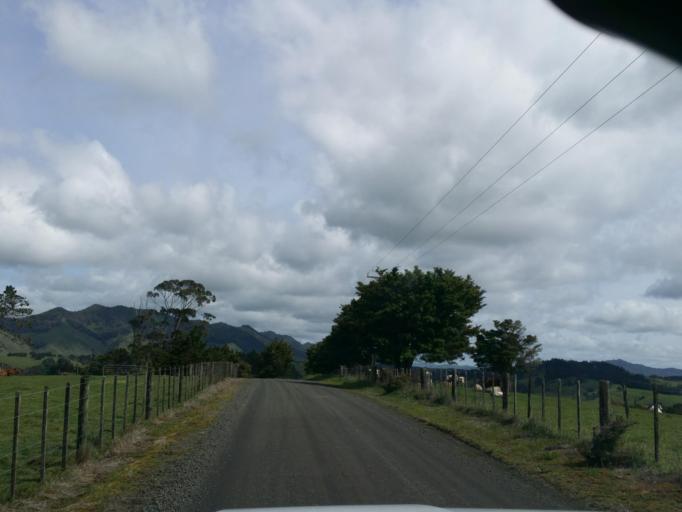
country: NZ
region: Northland
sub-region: Kaipara District
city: Dargaville
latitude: -35.8378
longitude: 174.0281
